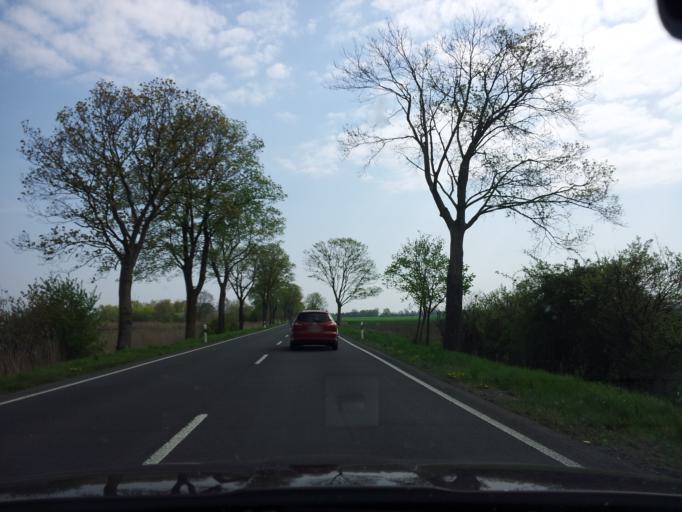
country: DE
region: Brandenburg
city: Golzow
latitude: 52.5424
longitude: 14.4461
